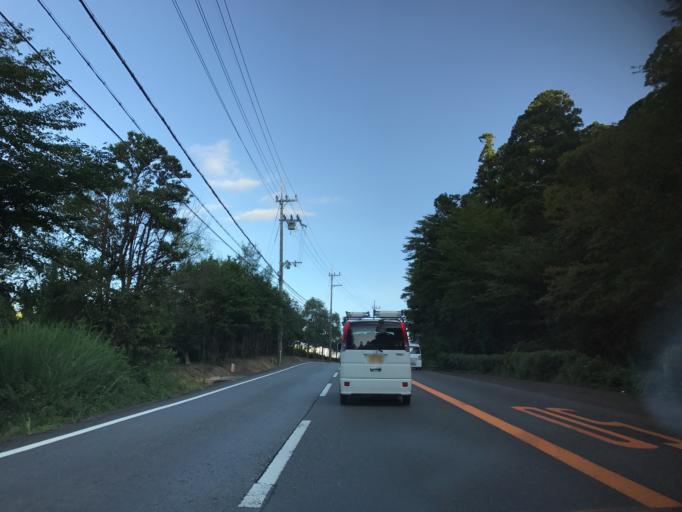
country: JP
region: Shiga Prefecture
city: Youkaichi
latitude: 35.0694
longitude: 136.2487
